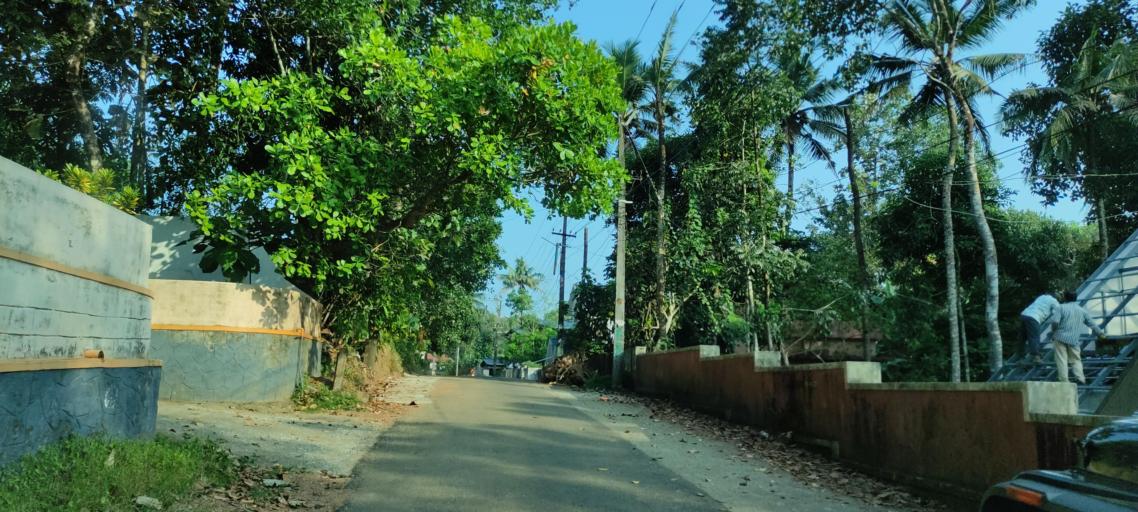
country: IN
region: Kerala
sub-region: Pattanamtitta
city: Adur
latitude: 9.1547
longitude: 76.7462
